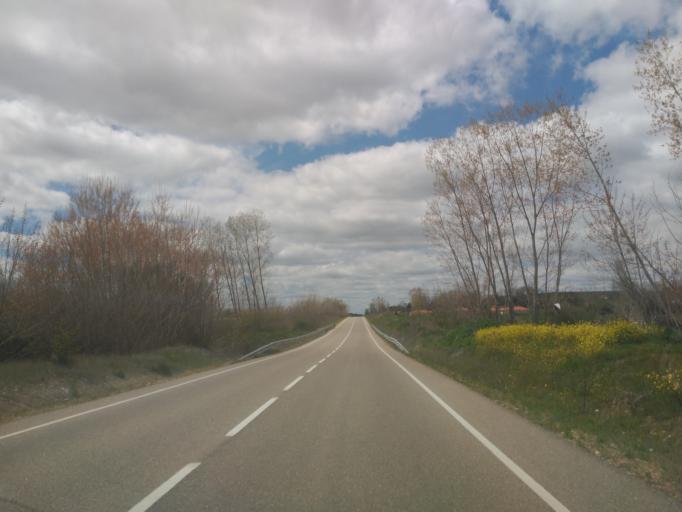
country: ES
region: Castille and Leon
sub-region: Provincia de Salamanca
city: Valverdon
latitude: 41.0484
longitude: -5.7753
